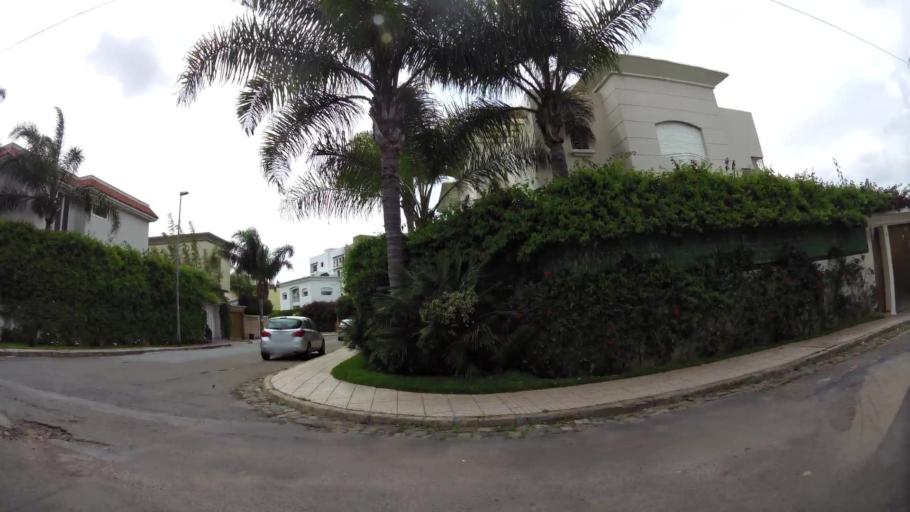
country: MA
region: Grand Casablanca
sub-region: Casablanca
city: Casablanca
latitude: 33.5551
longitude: -7.6432
